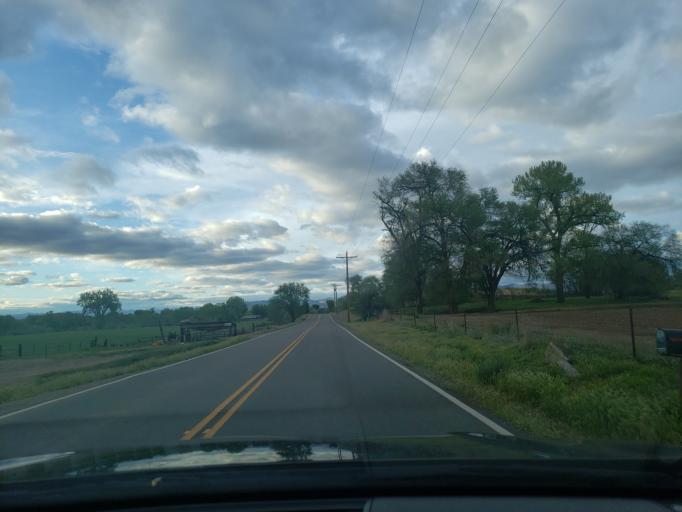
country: US
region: Colorado
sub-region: Mesa County
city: Fruita
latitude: 39.2008
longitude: -108.7291
